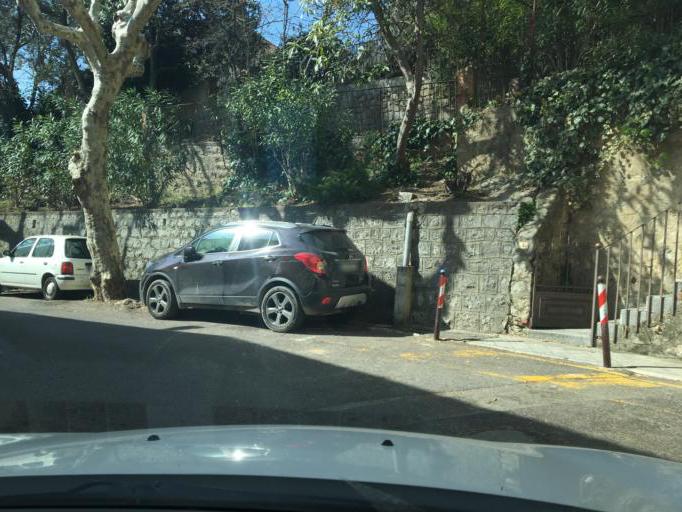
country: FR
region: Provence-Alpes-Cote d'Azur
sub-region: Departement du Var
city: Bargemon
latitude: 43.6198
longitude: 6.5500
